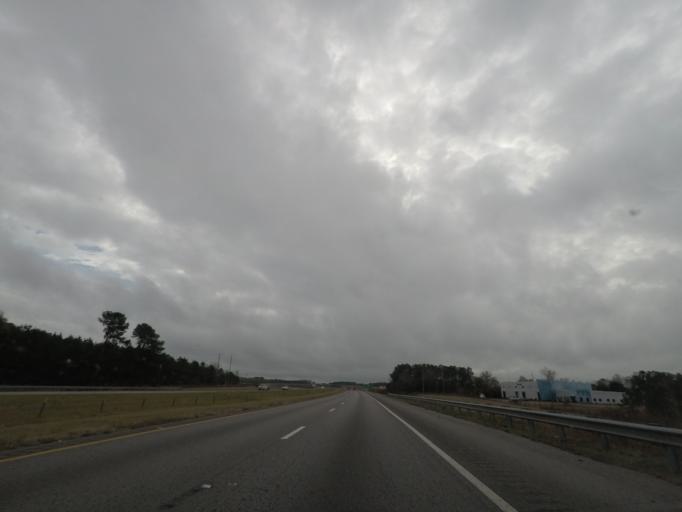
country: US
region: South Carolina
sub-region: Orangeburg County
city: Holly Hill
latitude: 33.4709
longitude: -80.4765
